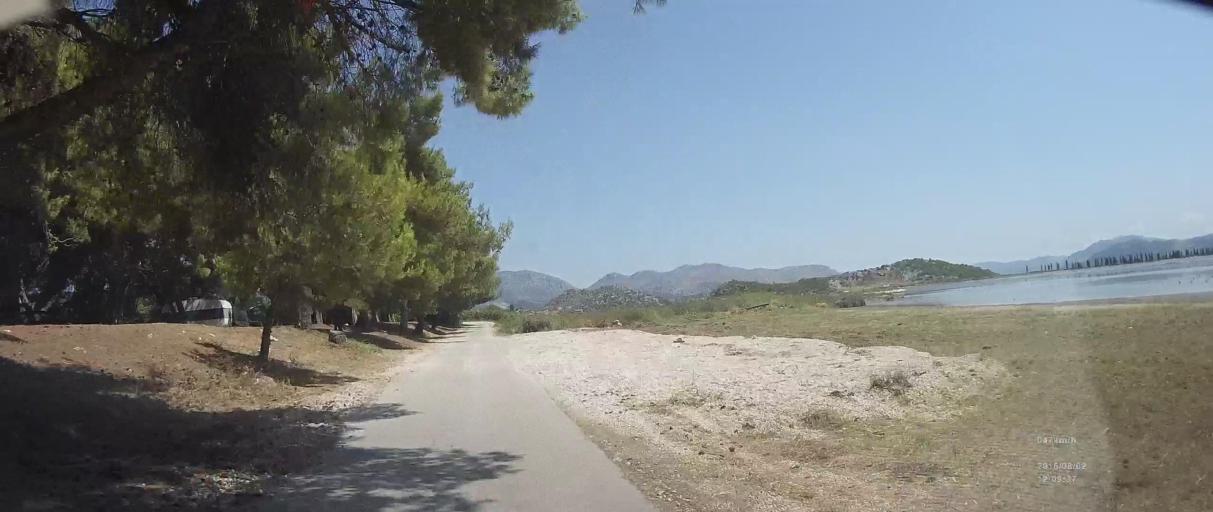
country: HR
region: Dubrovacko-Neretvanska
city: Komin
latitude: 43.0220
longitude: 17.4516
